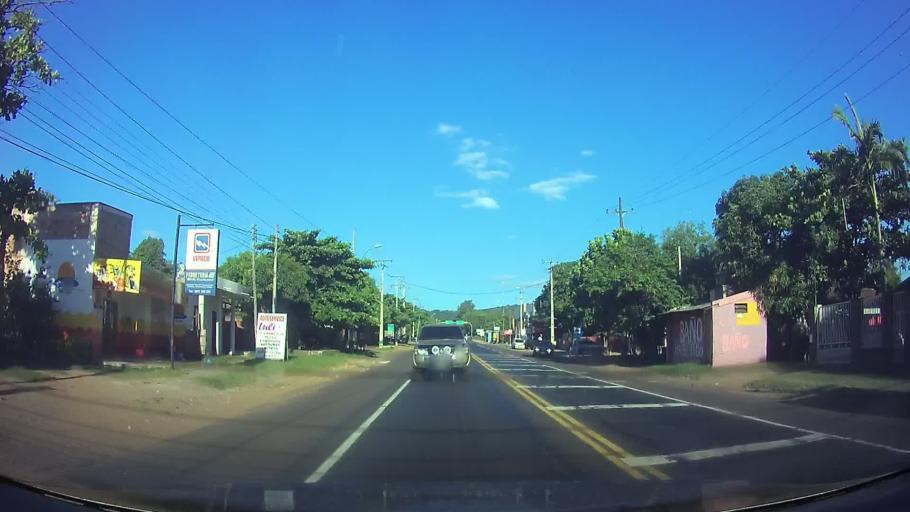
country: PY
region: Central
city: Ypacarai
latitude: -25.3729
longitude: -57.2215
